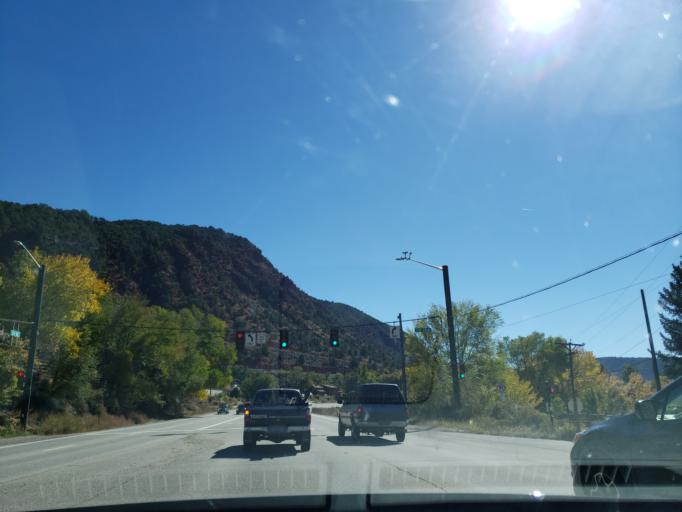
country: US
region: Colorado
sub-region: Garfield County
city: Glenwood Springs
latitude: 39.5059
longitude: -107.3031
